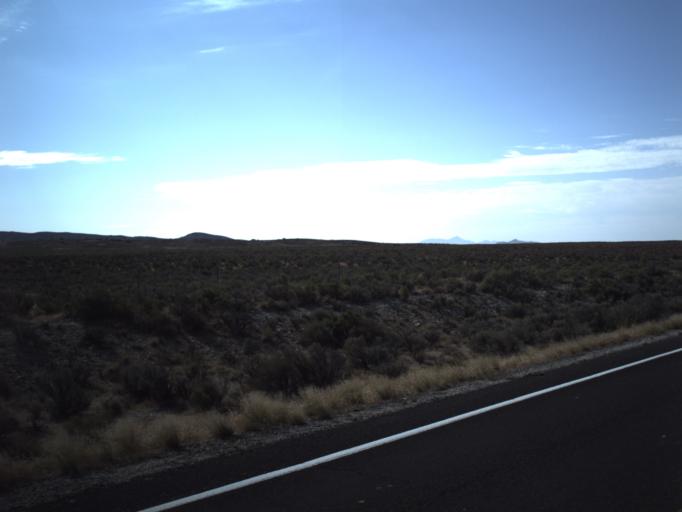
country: US
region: Idaho
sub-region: Cassia County
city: Burley
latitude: 41.6688
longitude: -113.5450
